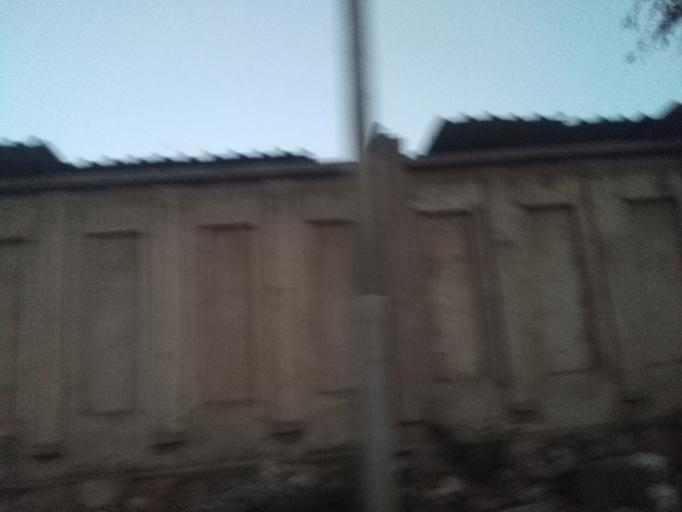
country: TZ
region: Dar es Salaam
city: Magomeni
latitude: -6.7645
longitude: 39.2801
